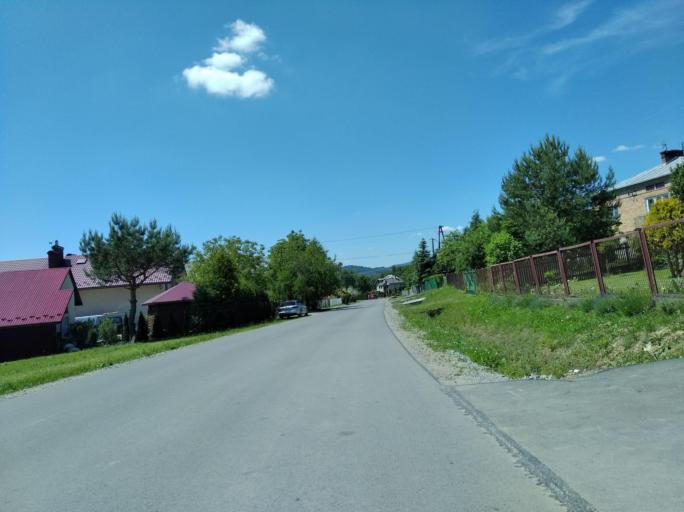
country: PL
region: Subcarpathian Voivodeship
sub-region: Powiat jasielski
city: Nowy Zmigrod
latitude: 49.6188
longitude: 21.5812
